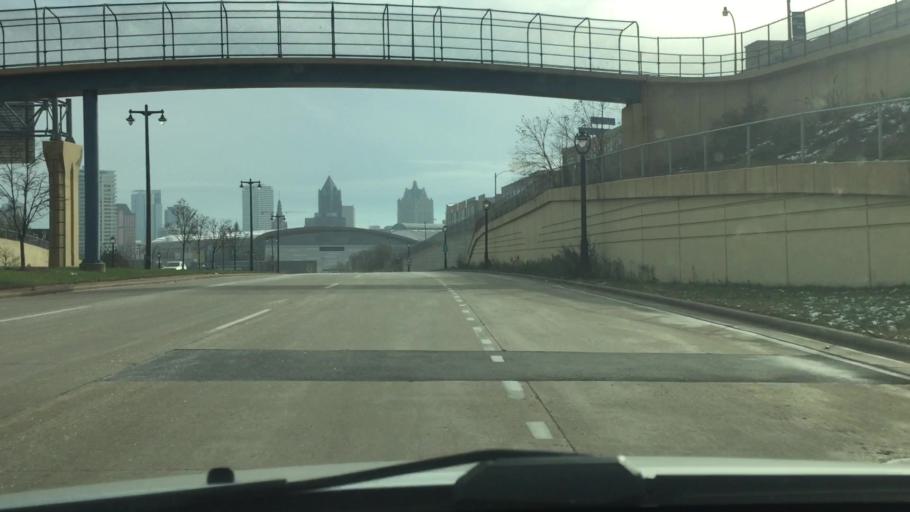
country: US
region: Wisconsin
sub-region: Milwaukee County
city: Milwaukee
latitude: 43.0480
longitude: -87.9240
